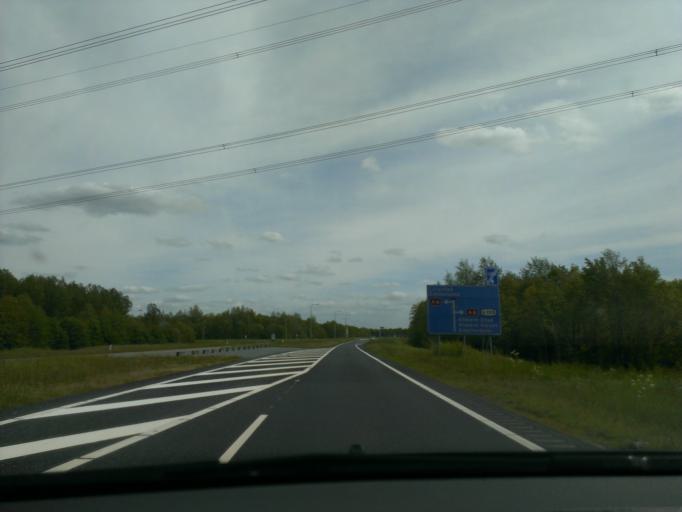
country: NL
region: Flevoland
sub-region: Gemeente Almere
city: Almere Stad
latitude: 52.4021
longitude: 5.3393
